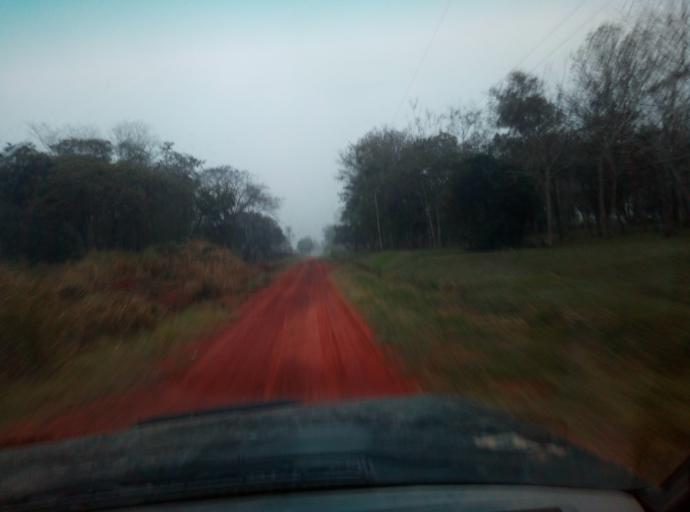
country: PY
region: Caaguazu
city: Doctor Cecilio Baez
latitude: -25.1568
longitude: -56.2770
